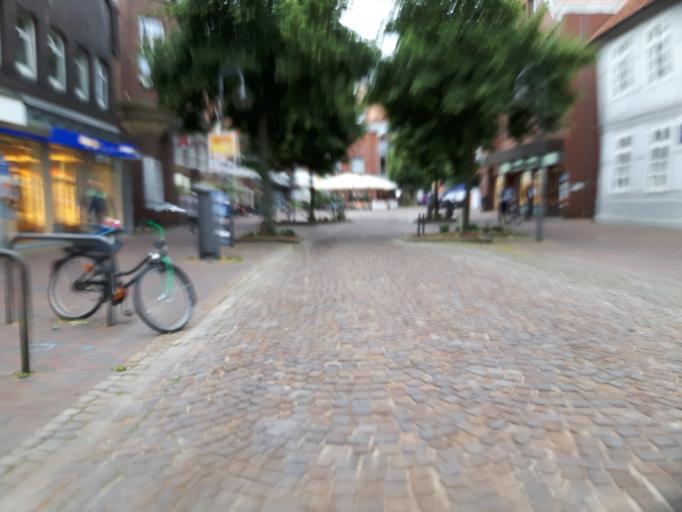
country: DE
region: Lower Saxony
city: Winsen
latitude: 53.3636
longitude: 10.2075
